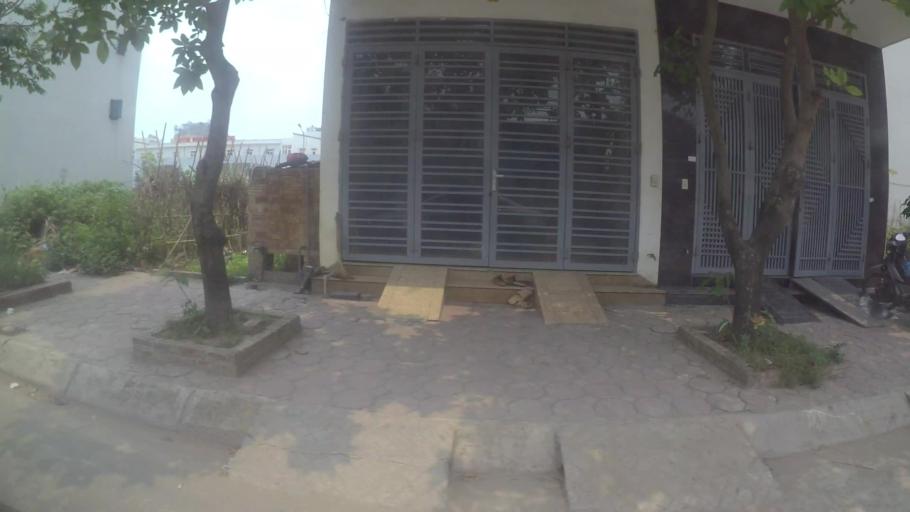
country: VN
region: Ha Noi
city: Ha Dong
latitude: 20.9890
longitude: 105.7431
